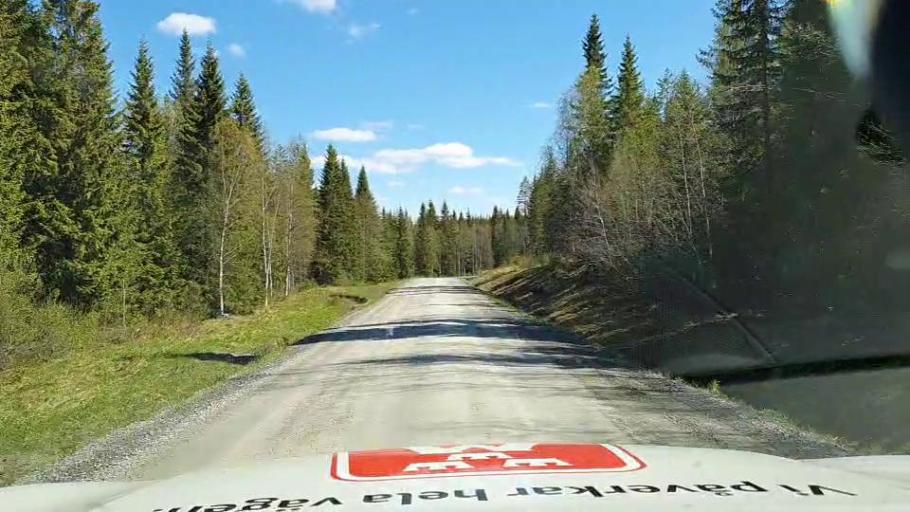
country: SE
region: Jaemtland
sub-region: Krokoms Kommun
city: Valla
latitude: 63.6660
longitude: 13.7165
